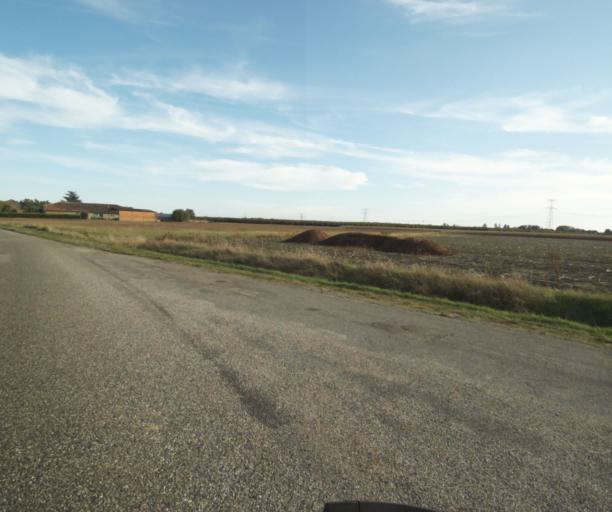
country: FR
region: Midi-Pyrenees
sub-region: Departement du Tarn-et-Garonne
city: Finhan
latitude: 43.9056
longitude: 1.1188
